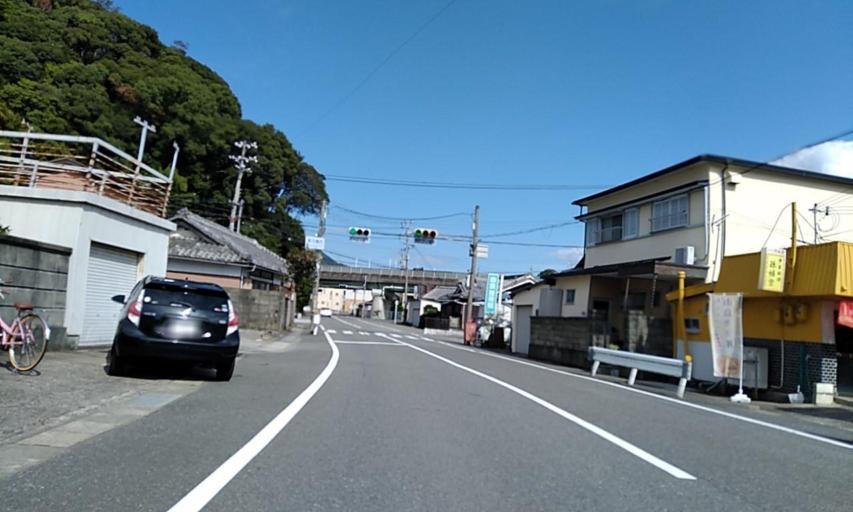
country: JP
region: Wakayama
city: Gobo
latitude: 33.9607
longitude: 135.1227
